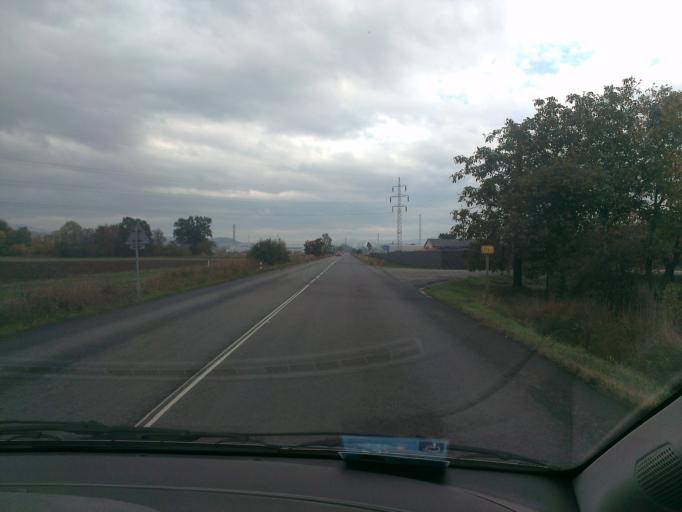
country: CZ
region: Zlin
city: Lesna
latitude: 49.5089
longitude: 17.9293
